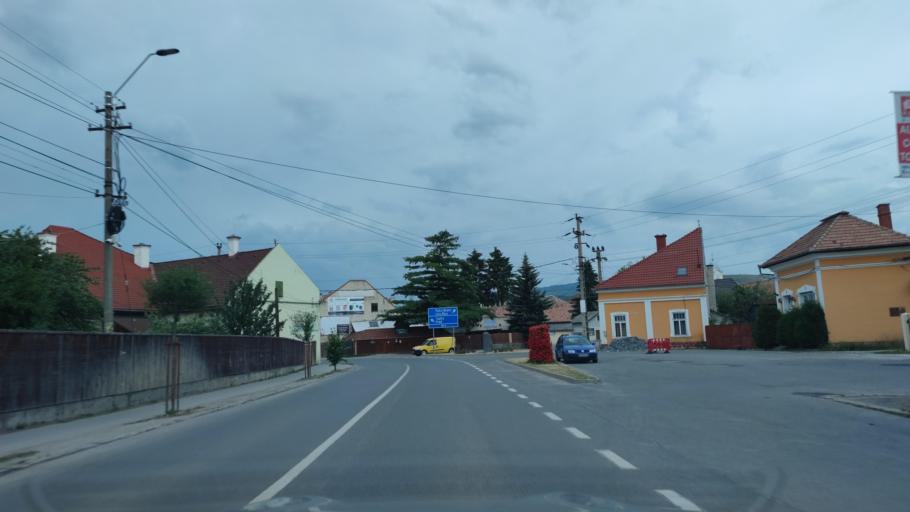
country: RO
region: Harghita
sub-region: Municipiul Gheorgheni
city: Gheorgheni
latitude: 46.7193
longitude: 25.6020
